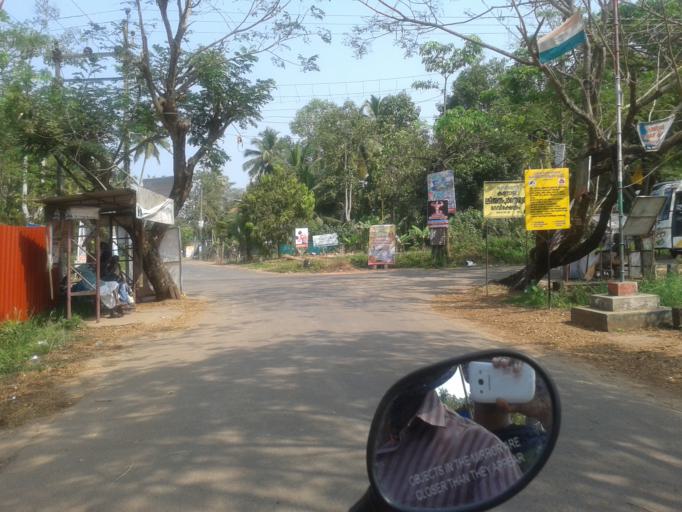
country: IN
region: Kerala
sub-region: Kottayam
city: Changanacheri
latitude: 9.4622
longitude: 76.4501
